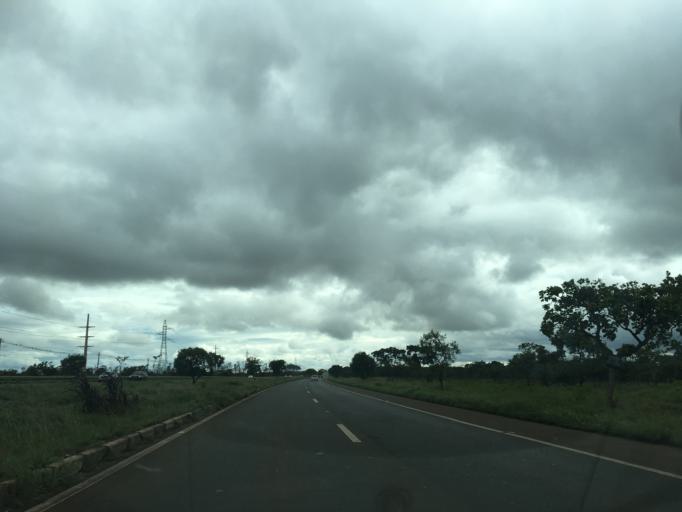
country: BR
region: Federal District
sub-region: Brasilia
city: Brasilia
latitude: -15.9090
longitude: -47.8218
